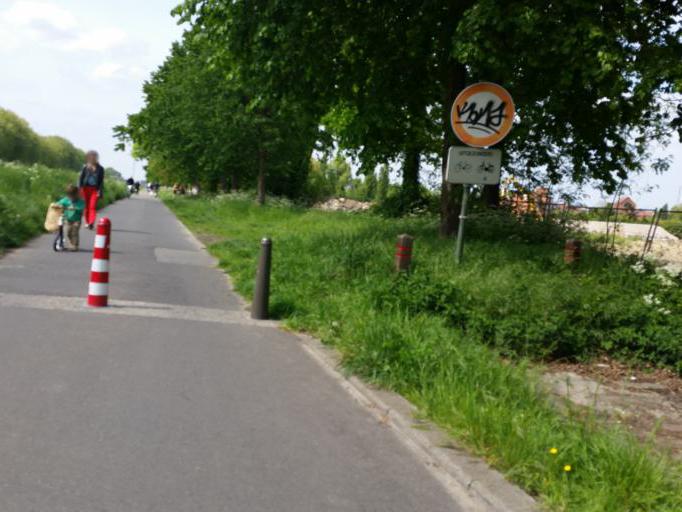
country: BE
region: Flanders
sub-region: Provincie Antwerpen
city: Mechelen
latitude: 51.0231
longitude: 4.4694
